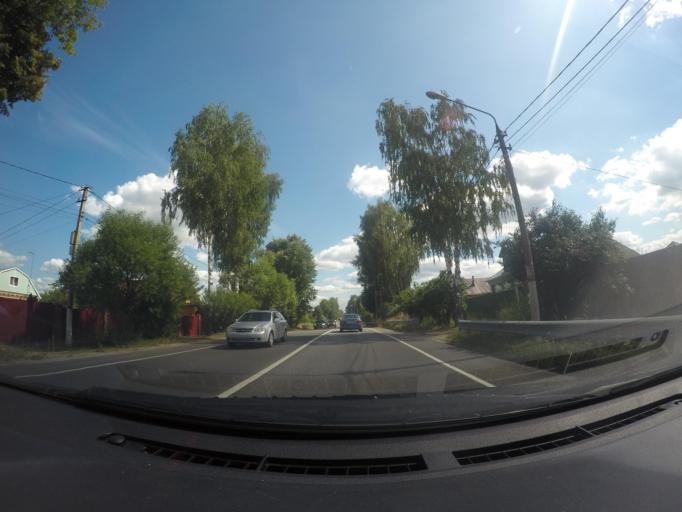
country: RU
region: Moskovskaya
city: Gzhel'
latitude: 55.6140
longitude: 38.3888
